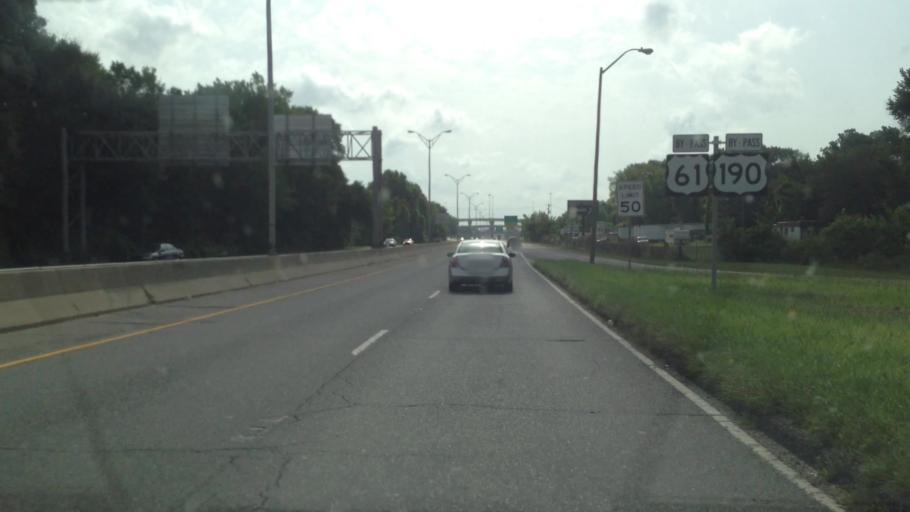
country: US
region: Louisiana
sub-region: East Baton Rouge Parish
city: Baton Rouge
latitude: 30.5085
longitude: -91.1698
